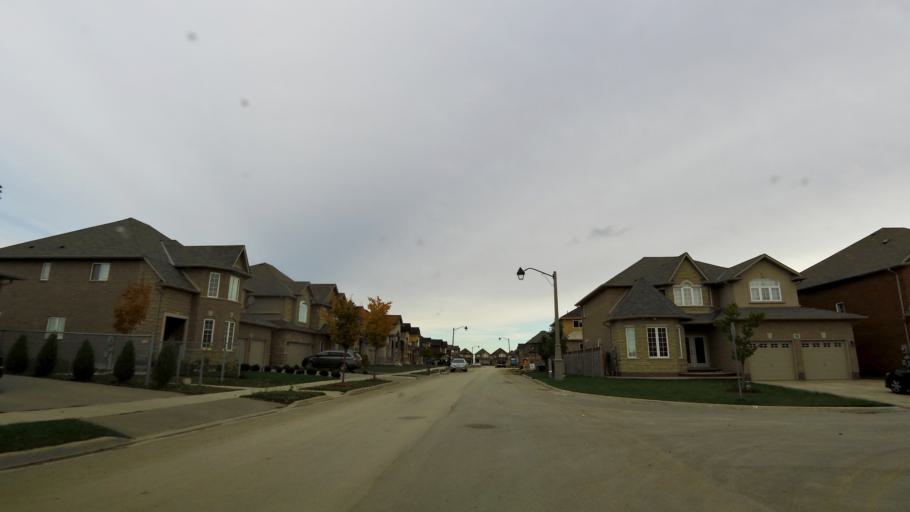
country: CA
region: Ontario
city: Hamilton
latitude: 43.1755
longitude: -79.8054
